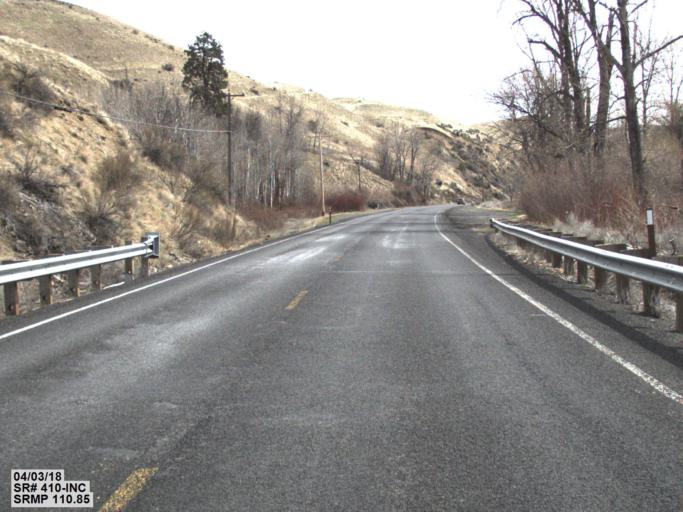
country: US
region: Washington
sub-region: Yakima County
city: Tieton
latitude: 46.7913
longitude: -120.8734
